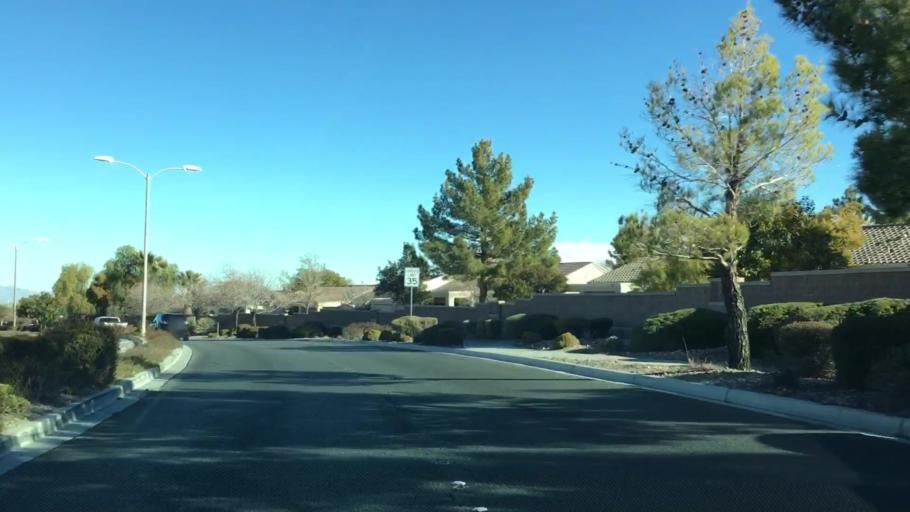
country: US
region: Nevada
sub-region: Clark County
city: Whitney
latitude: 35.9691
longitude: -115.1011
